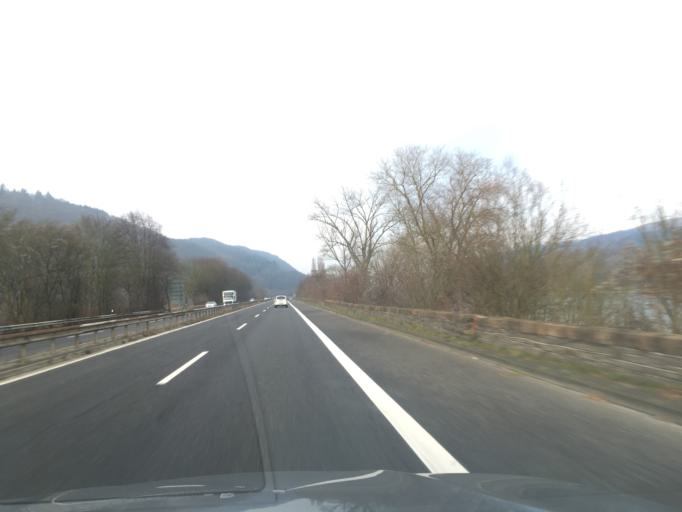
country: DE
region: Rheinland-Pfalz
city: Hammerstein
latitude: 50.4622
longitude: 7.3572
